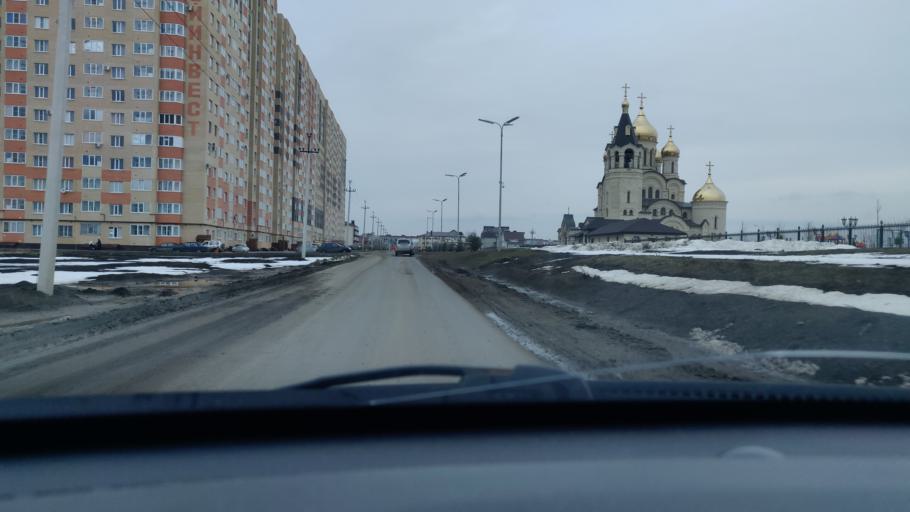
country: RU
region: Stavropol'skiy
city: Tatarka
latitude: 45.0102
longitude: 41.8994
